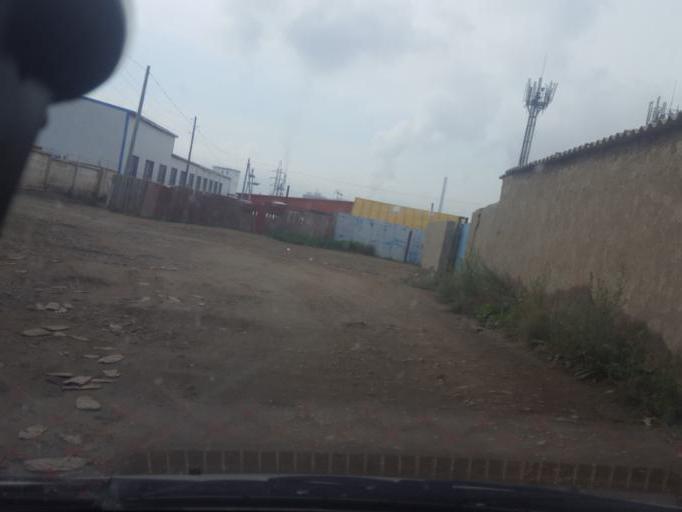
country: MN
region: Ulaanbaatar
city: Ulaanbaatar
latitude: 47.9192
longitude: 106.7990
